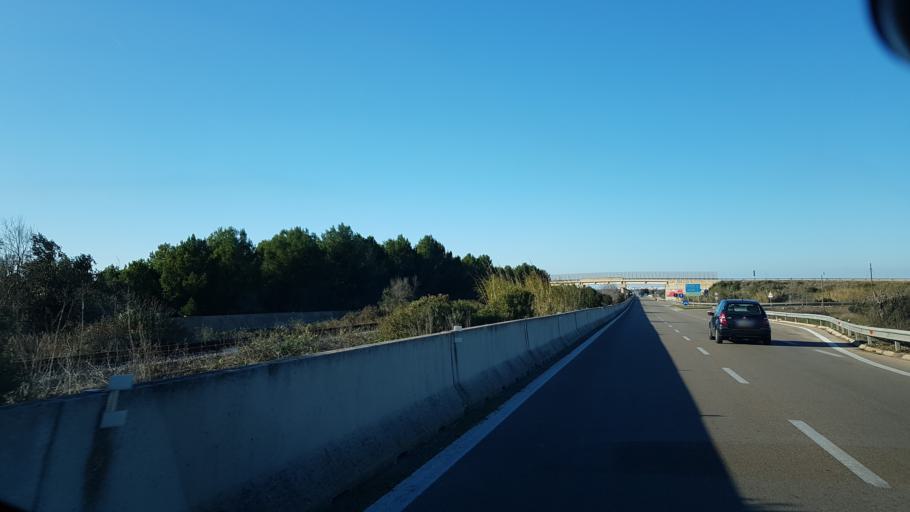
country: IT
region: Apulia
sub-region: Provincia di Lecce
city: Taviano
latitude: 40.0100
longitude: 18.0536
